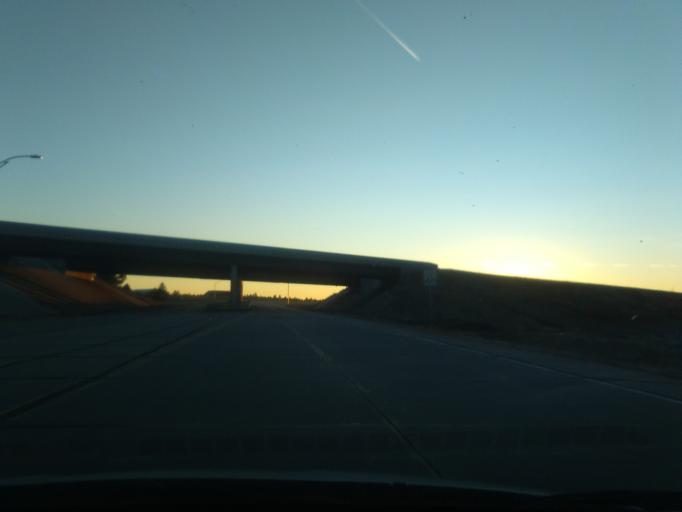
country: US
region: Nebraska
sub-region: Cheyenne County
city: Sidney
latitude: 41.1141
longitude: -102.9729
